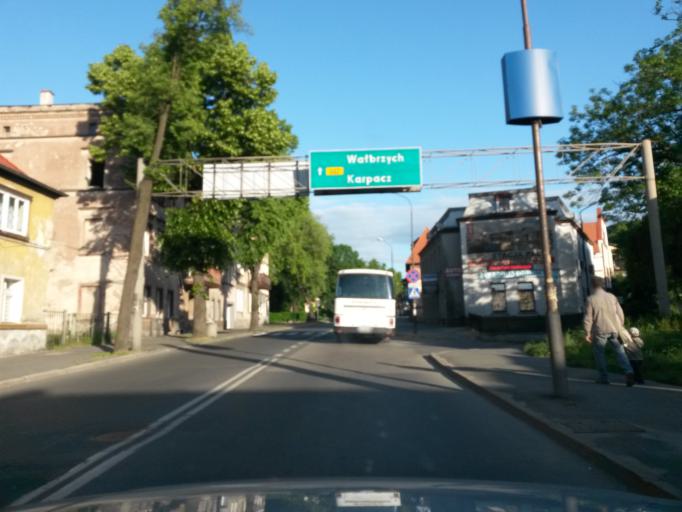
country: PL
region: Lower Silesian Voivodeship
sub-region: Jelenia Gora
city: Jelenia Gora
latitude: 50.8987
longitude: 15.7409
